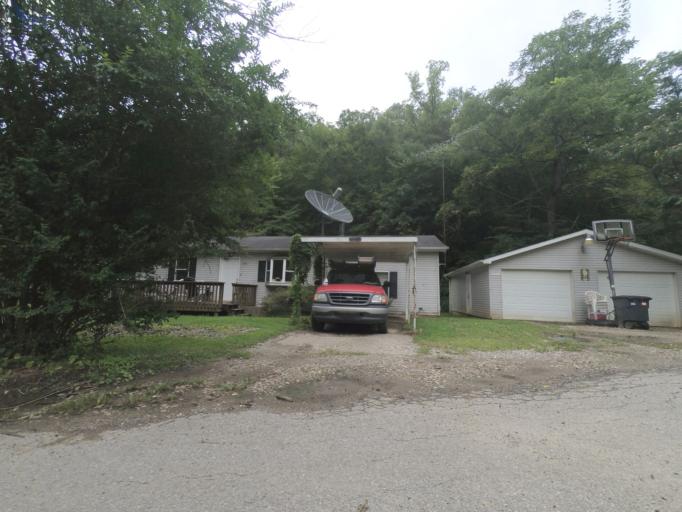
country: US
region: West Virginia
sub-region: Cabell County
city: Huntington
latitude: 38.3833
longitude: -82.4327
